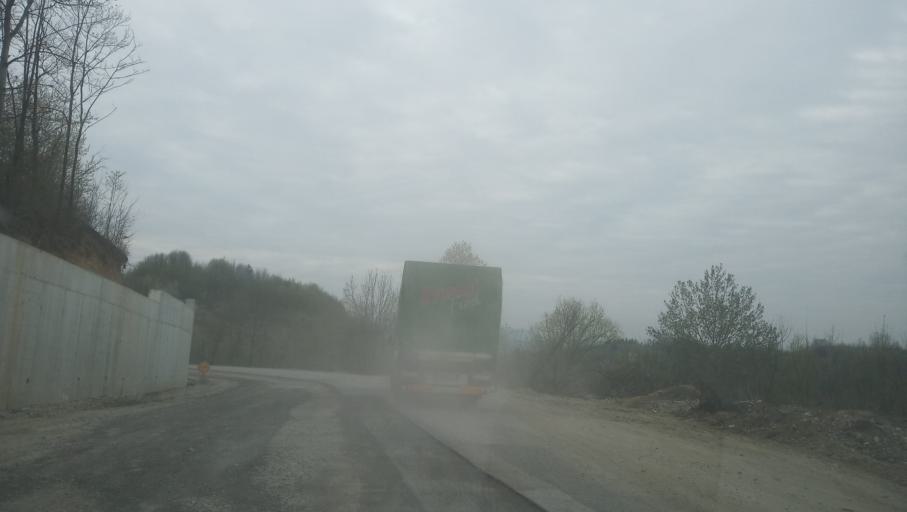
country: RO
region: Arad
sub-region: Comuna Varfurile
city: Varfurile
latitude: 46.3454
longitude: 22.5510
